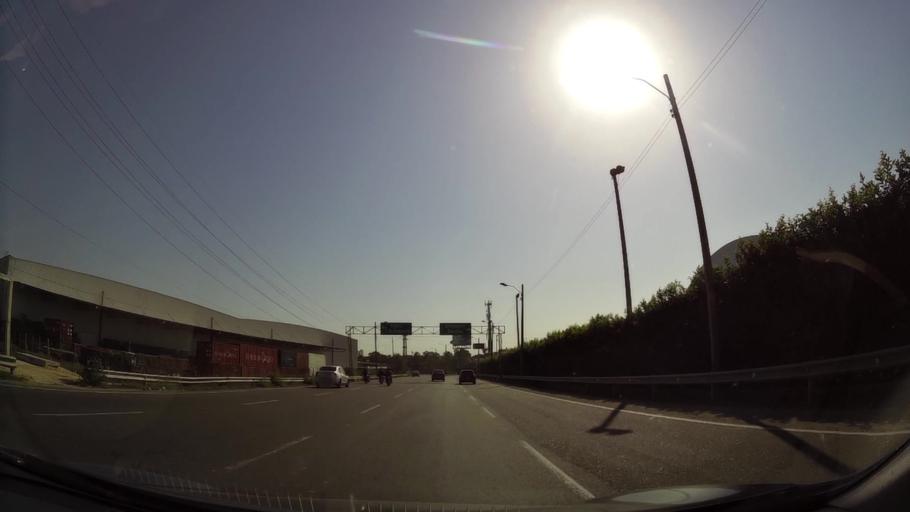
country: CO
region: Bolivar
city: Cartagena
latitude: 10.3803
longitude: -75.5044
